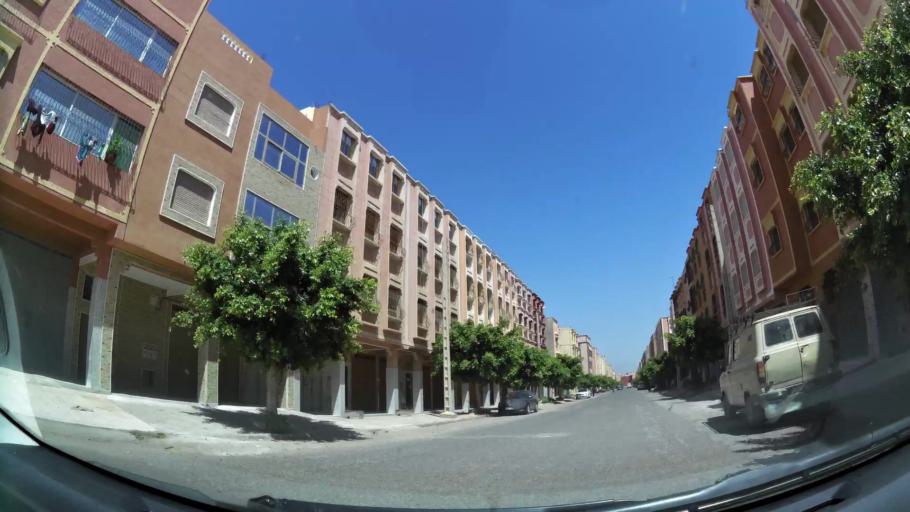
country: MA
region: Souss-Massa-Draa
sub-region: Inezgane-Ait Mellou
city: Inezgane
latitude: 30.3335
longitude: -9.5018
